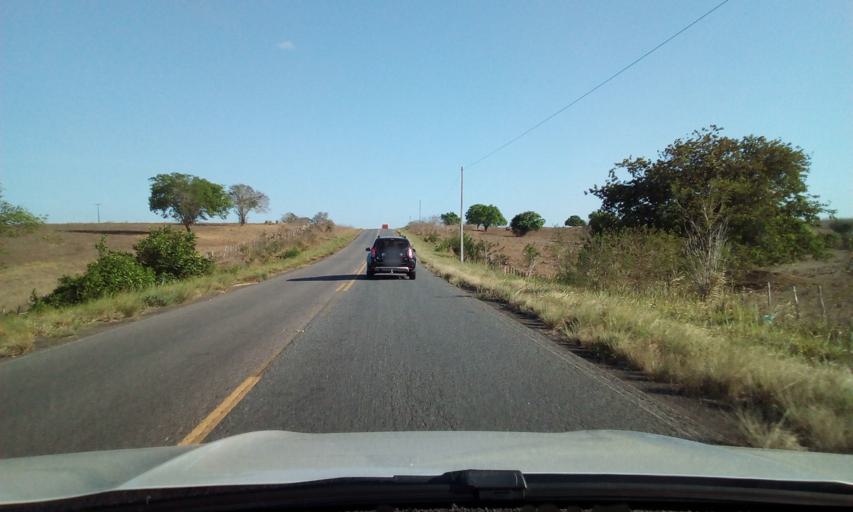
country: BR
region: Paraiba
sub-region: Mulungu
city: Mulungu
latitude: -6.9885
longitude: -35.3887
